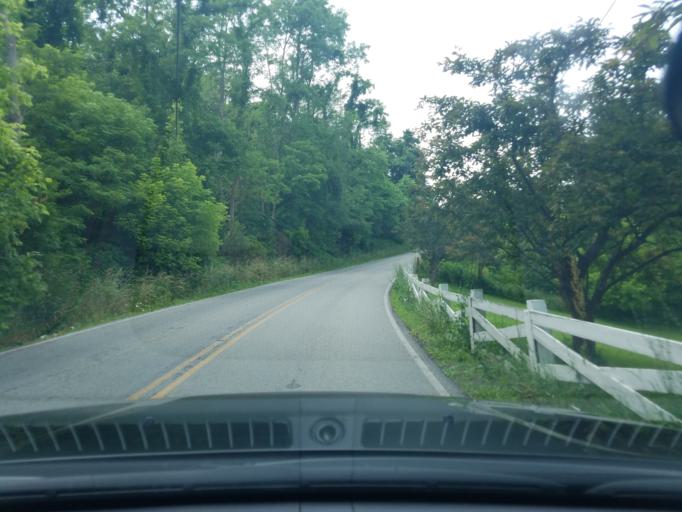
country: US
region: Pennsylvania
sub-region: Westmoreland County
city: Youngwood
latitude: 40.2190
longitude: -79.5568
